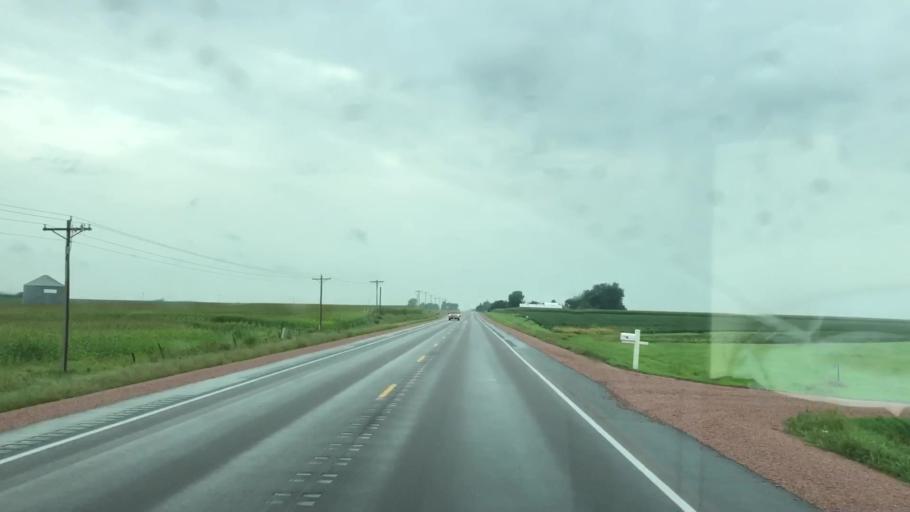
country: US
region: Iowa
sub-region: O'Brien County
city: Sanborn
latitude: 43.1861
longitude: -95.7281
